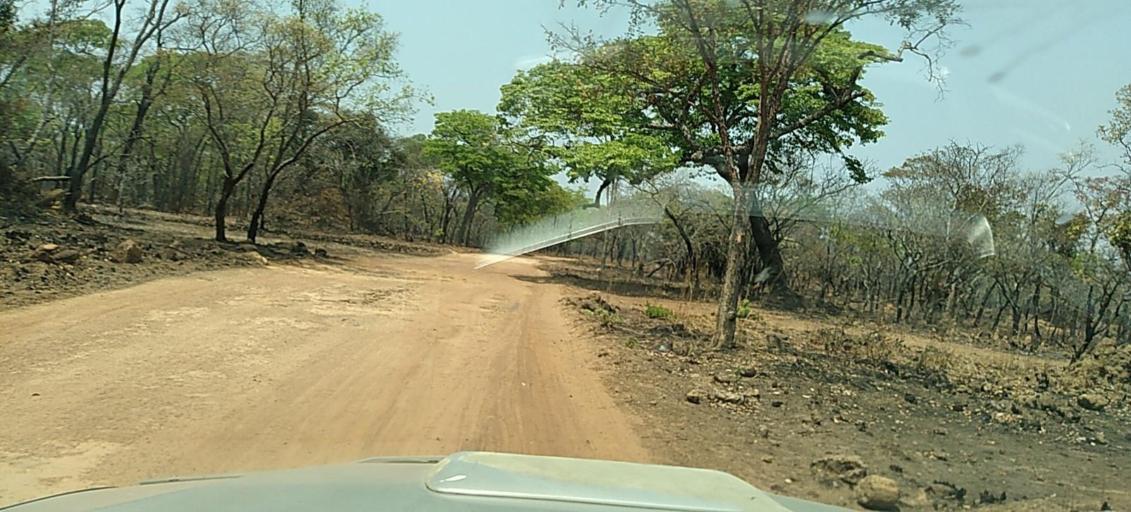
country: ZM
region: North-Western
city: Kasempa
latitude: -13.6075
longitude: 26.1837
